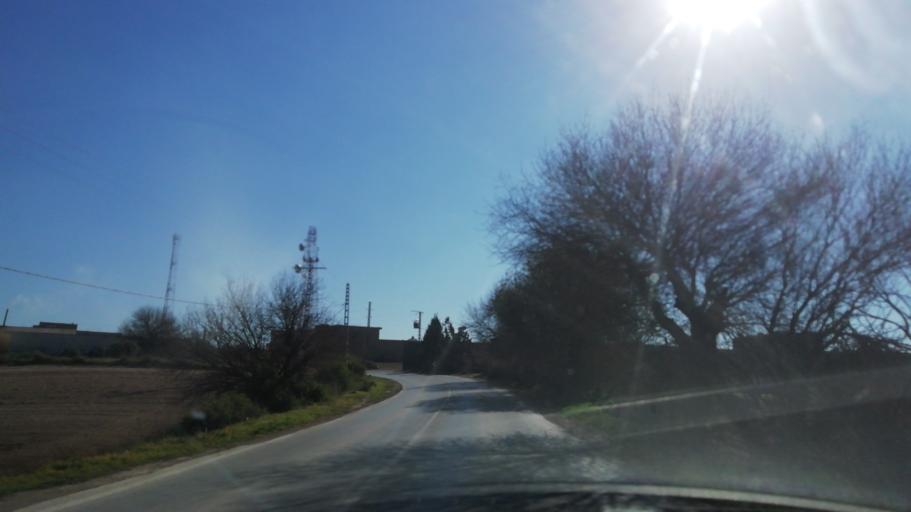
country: DZ
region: Tlemcen
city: Nedroma
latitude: 34.8376
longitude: -1.7027
